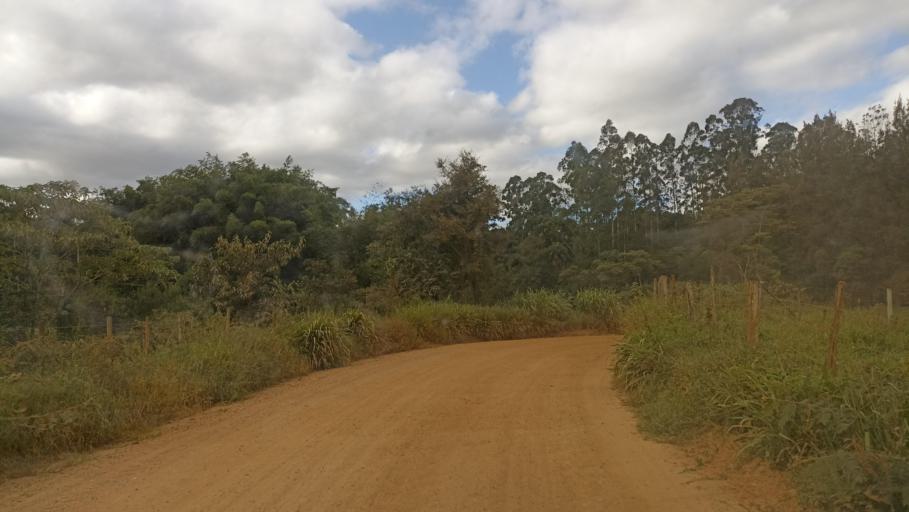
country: BR
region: Minas Gerais
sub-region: Tiradentes
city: Tiradentes
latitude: -21.0957
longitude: -44.0752
